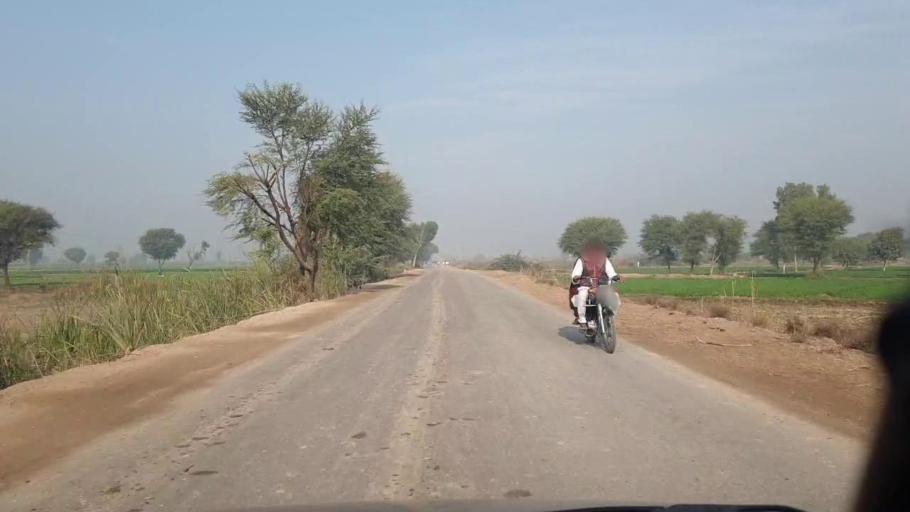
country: PK
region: Sindh
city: Shahdadpur
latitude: 25.9406
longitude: 68.6022
